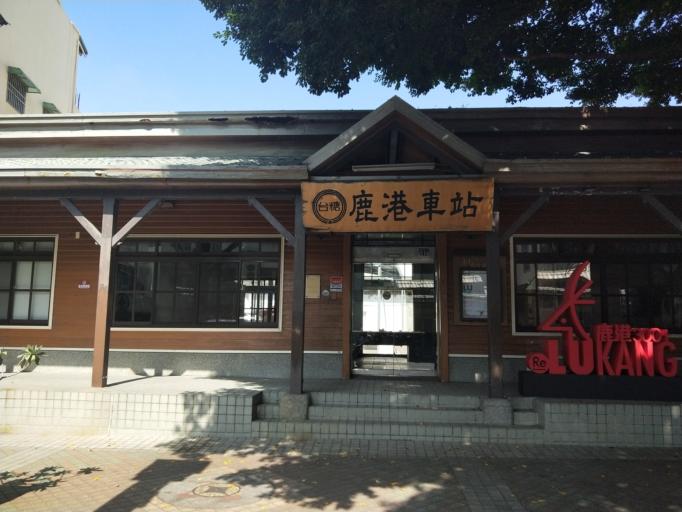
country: TW
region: Taiwan
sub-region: Changhua
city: Chang-hua
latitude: 24.0504
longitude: 120.4370
